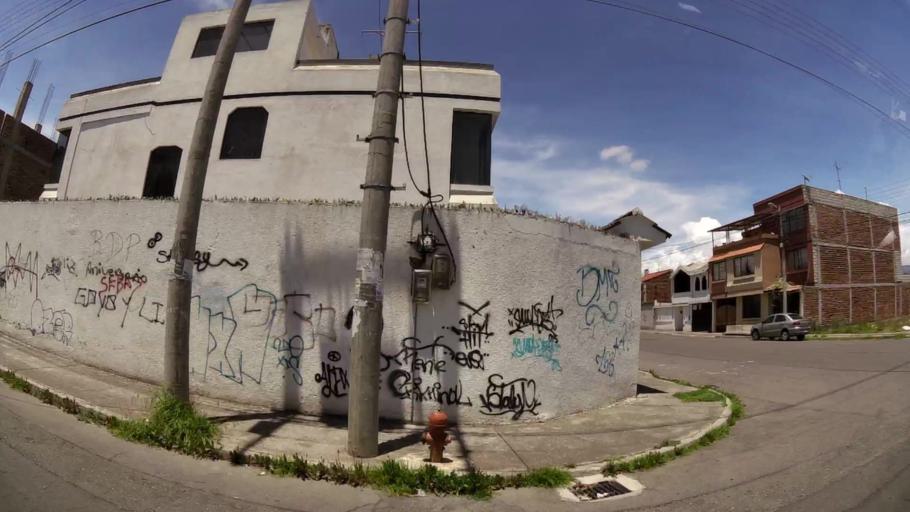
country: EC
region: Chimborazo
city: Riobamba
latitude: -1.6808
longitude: -78.6497
